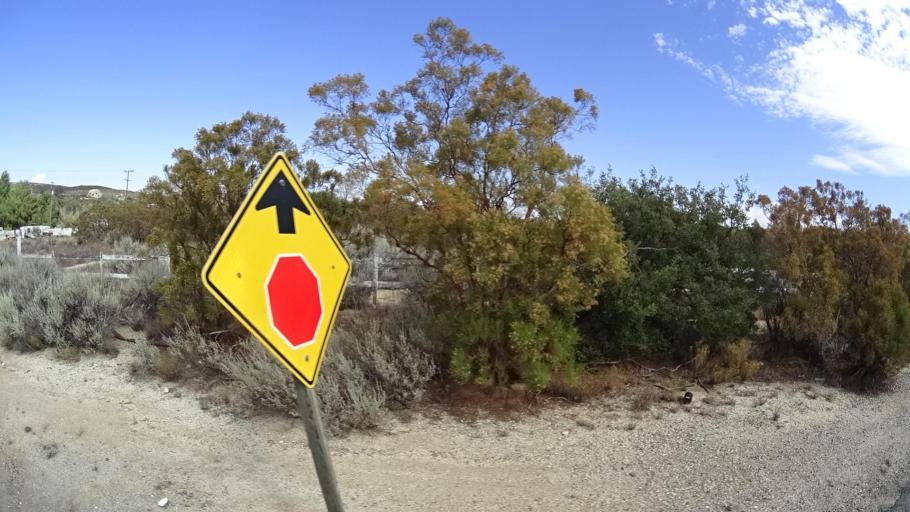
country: MX
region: Baja California
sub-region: Tecate
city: Cereso del Hongo
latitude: 32.6677
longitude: -116.2901
